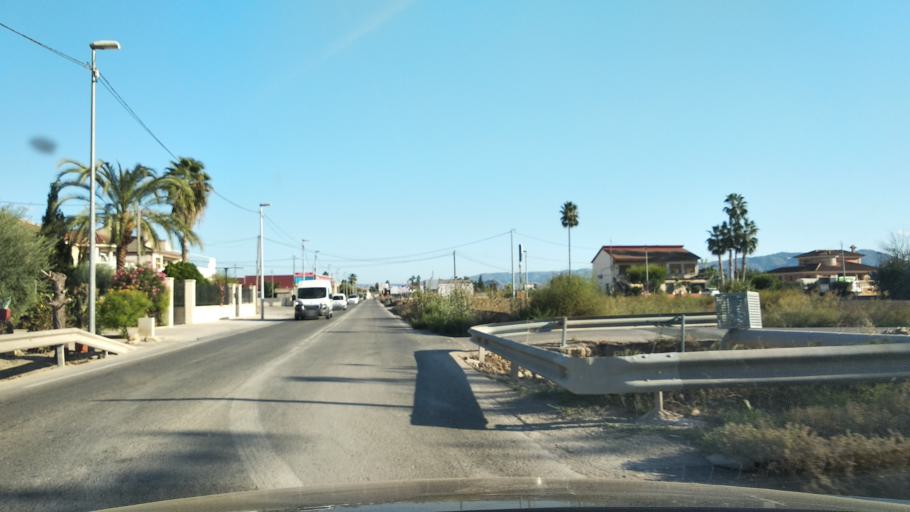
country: ES
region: Murcia
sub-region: Murcia
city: Santomera
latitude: 38.0448
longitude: -1.0530
